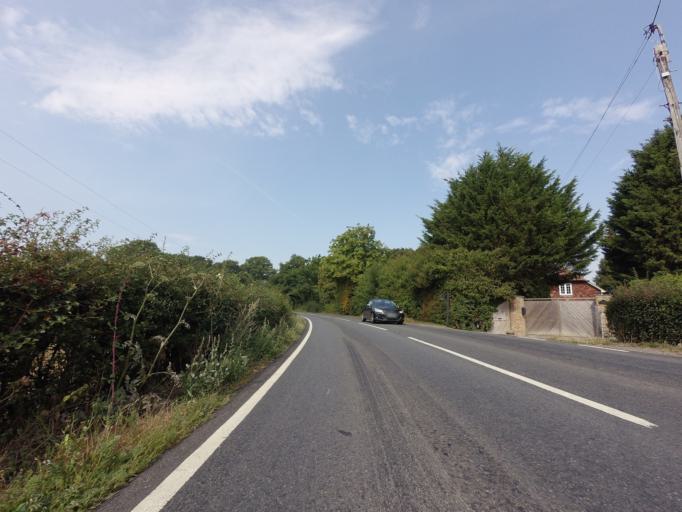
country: GB
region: England
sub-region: Kent
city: Headcorn
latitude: 51.1172
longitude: 0.6152
